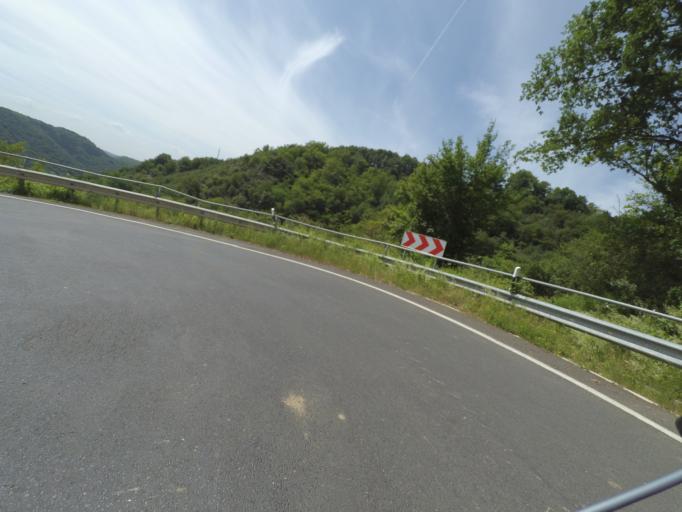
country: DE
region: Rheinland-Pfalz
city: Lutz
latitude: 50.1898
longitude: 7.3397
